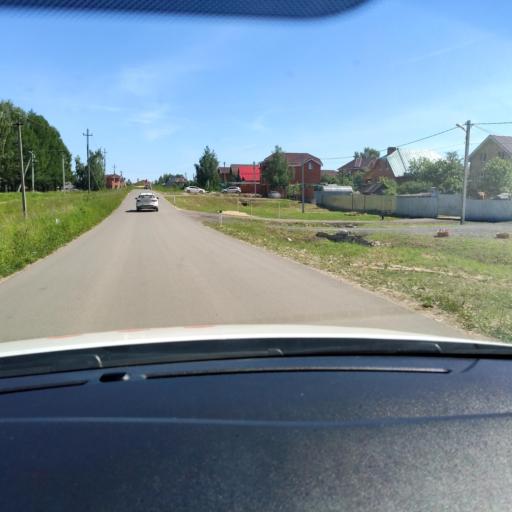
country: RU
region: Tatarstan
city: Staroye Arakchino
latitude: 55.8872
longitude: 49.0368
